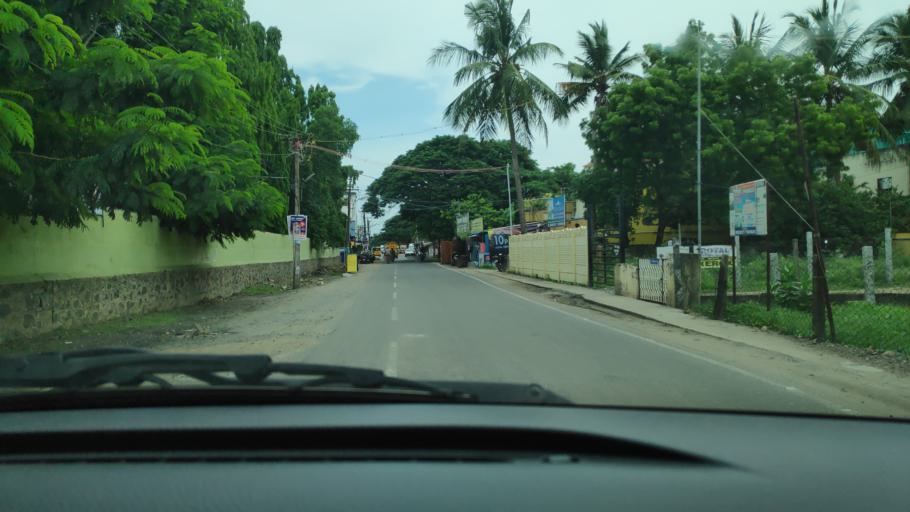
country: IN
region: Tamil Nadu
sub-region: Kancheepuram
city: Pallavaram
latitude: 12.9317
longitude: 80.1278
